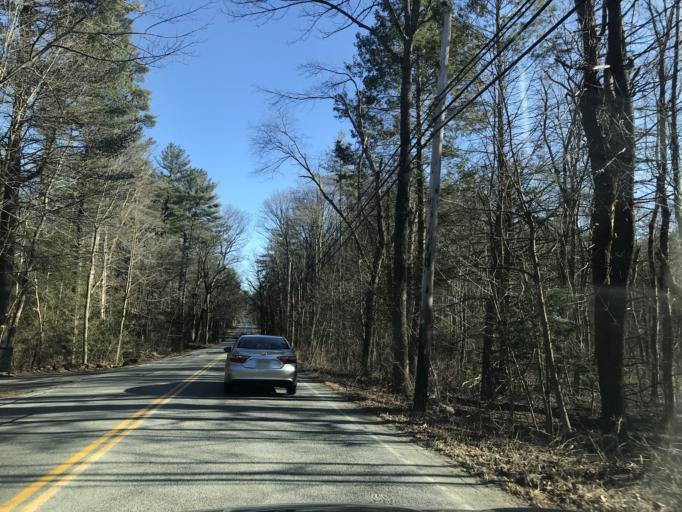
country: US
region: Massachusetts
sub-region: Essex County
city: Groveland
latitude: 42.7118
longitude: -71.0309
